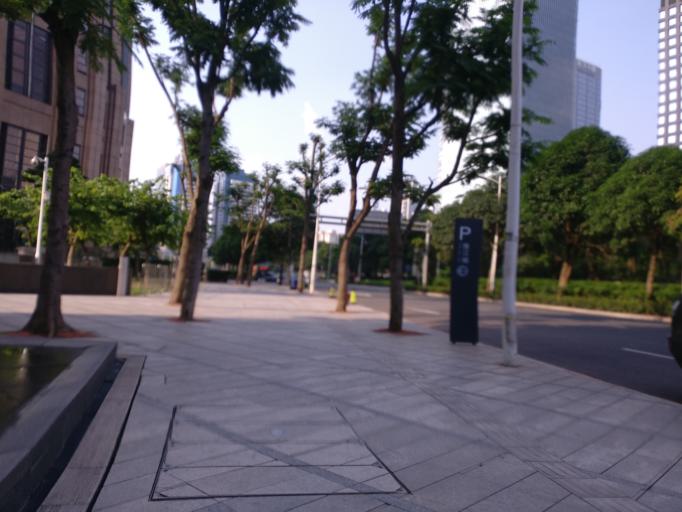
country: CN
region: Guangdong
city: Wushan
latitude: 23.1268
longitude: 113.3180
